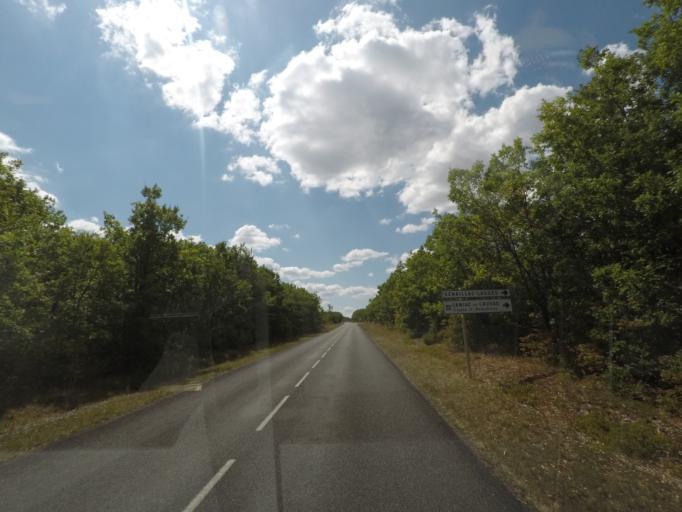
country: FR
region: Midi-Pyrenees
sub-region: Departement du Lot
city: Cajarc
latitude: 44.5799
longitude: 1.6939
